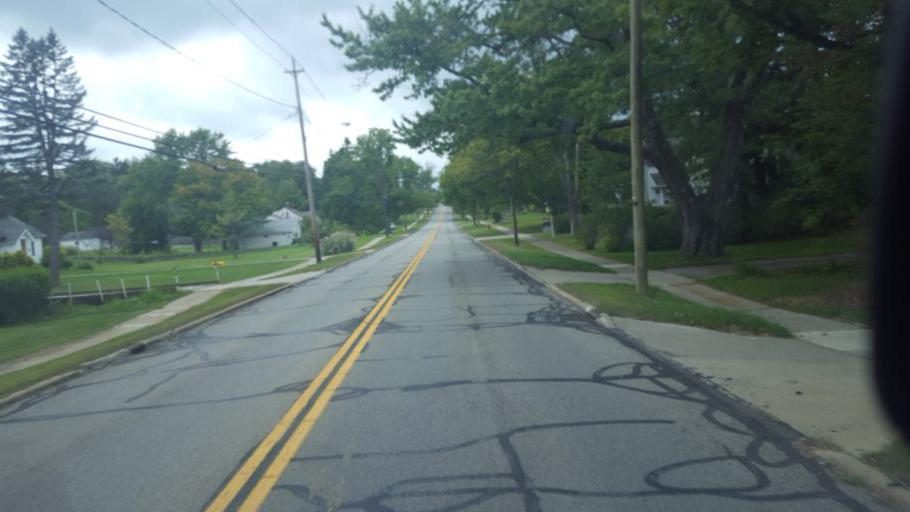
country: US
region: Ohio
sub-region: Geauga County
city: Chardon
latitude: 41.5836
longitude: -81.1931
